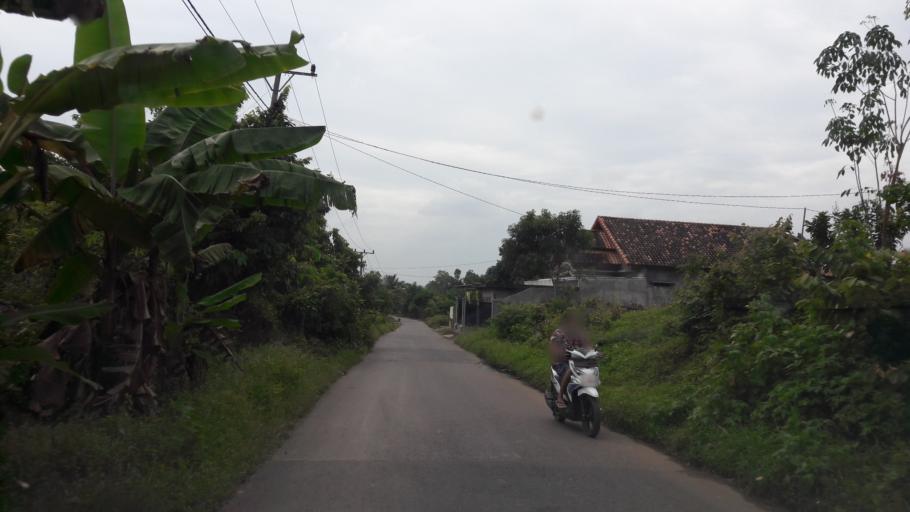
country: ID
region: South Sumatra
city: Gunungmenang
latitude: -3.1402
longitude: 104.1137
